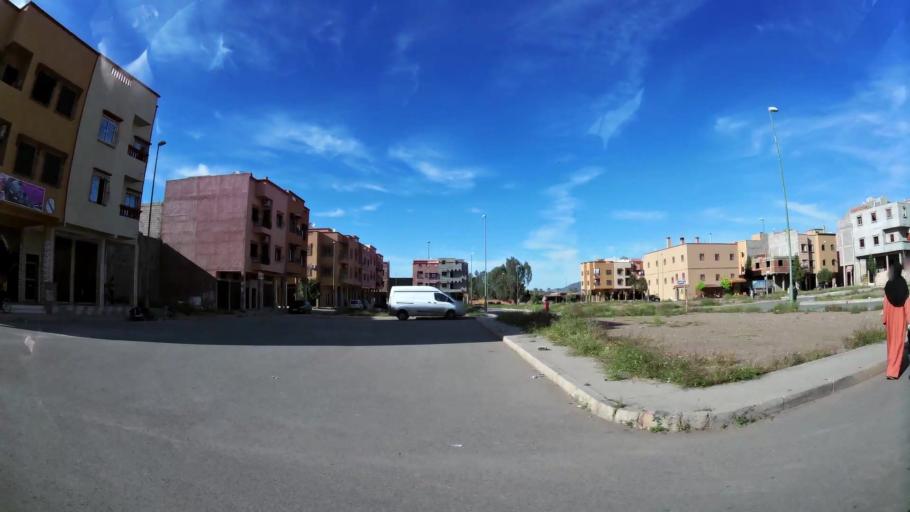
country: MA
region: Marrakech-Tensift-Al Haouz
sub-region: Marrakech
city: Marrakesh
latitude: 31.6895
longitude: -8.0726
